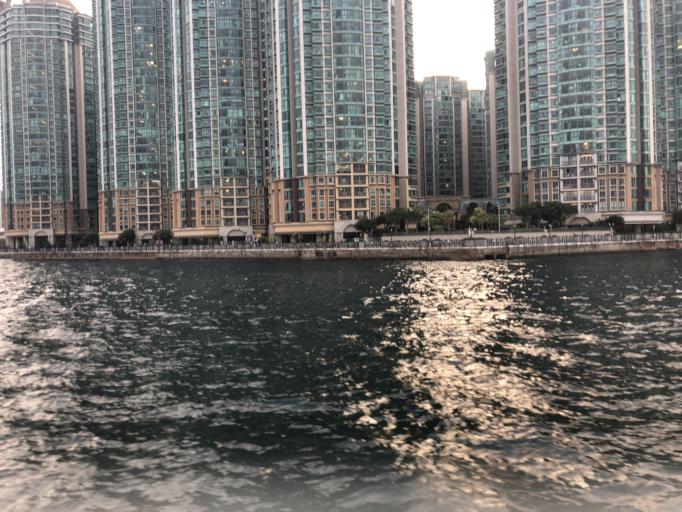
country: HK
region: Kowloon City
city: Kowloon
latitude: 22.3086
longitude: 114.1949
